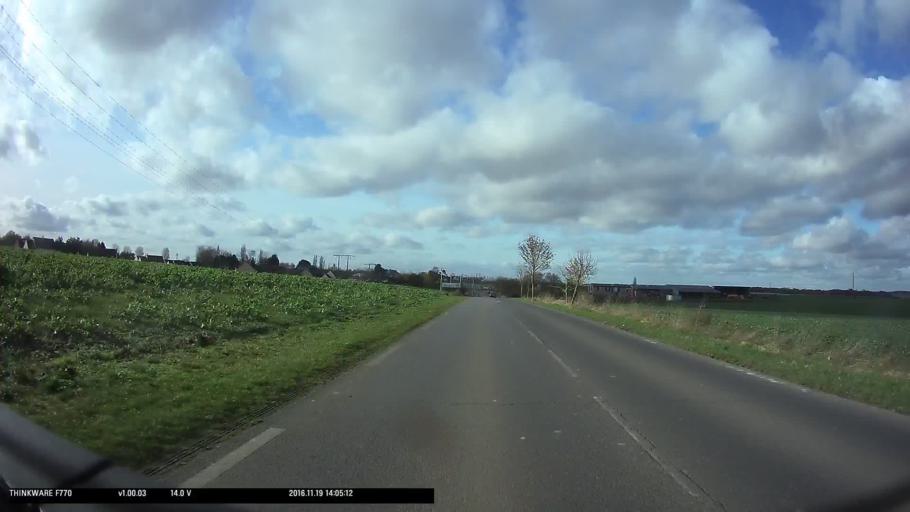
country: FR
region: Ile-de-France
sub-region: Departement du Val-d'Oise
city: Courdimanche
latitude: 49.0604
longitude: 2.0056
